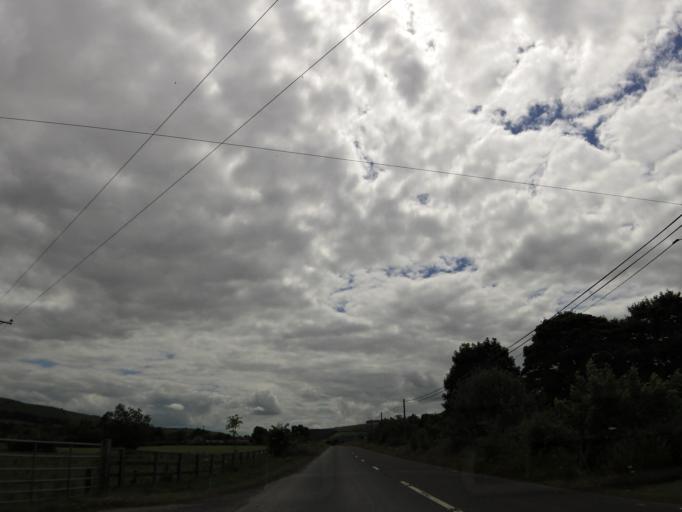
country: IE
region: Munster
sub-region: North Tipperary
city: Templemore
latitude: 52.7659
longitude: -8.0204
